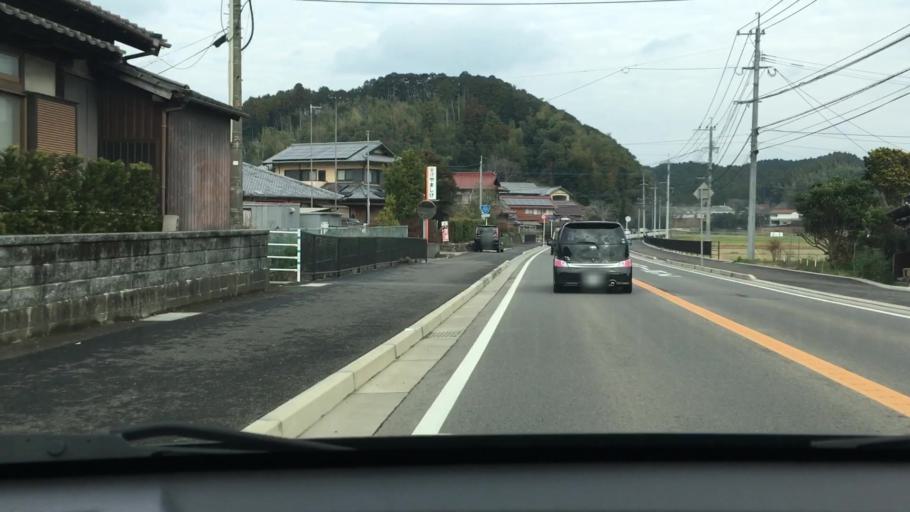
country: JP
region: Saga Prefecture
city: Imaricho-ko
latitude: 33.2956
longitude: 129.9147
